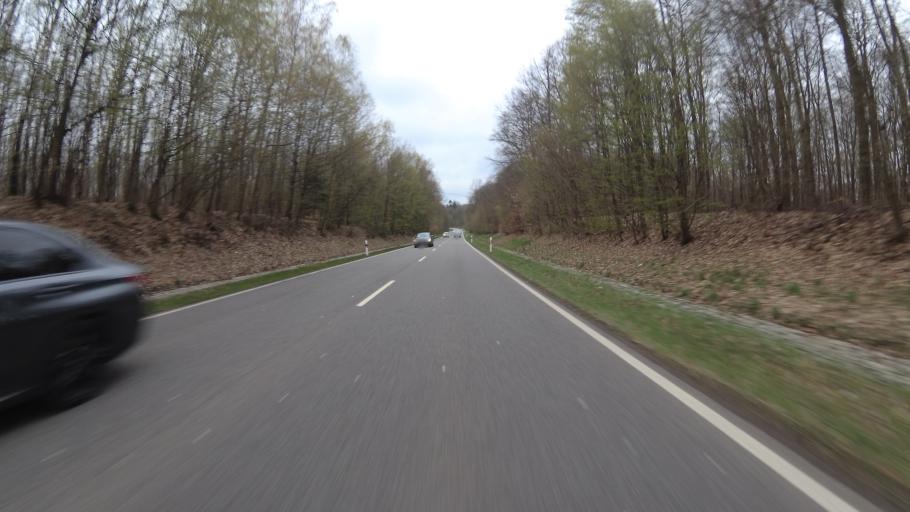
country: DE
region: Saarland
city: Merchweiler
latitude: 49.3467
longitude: 7.0766
